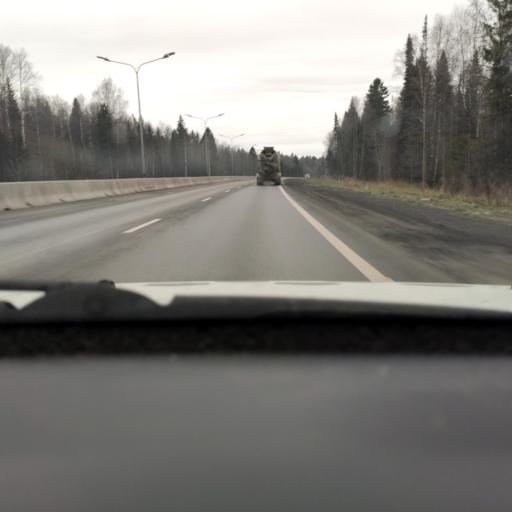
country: RU
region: Perm
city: Novyye Lyady
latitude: 58.0725
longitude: 56.4314
